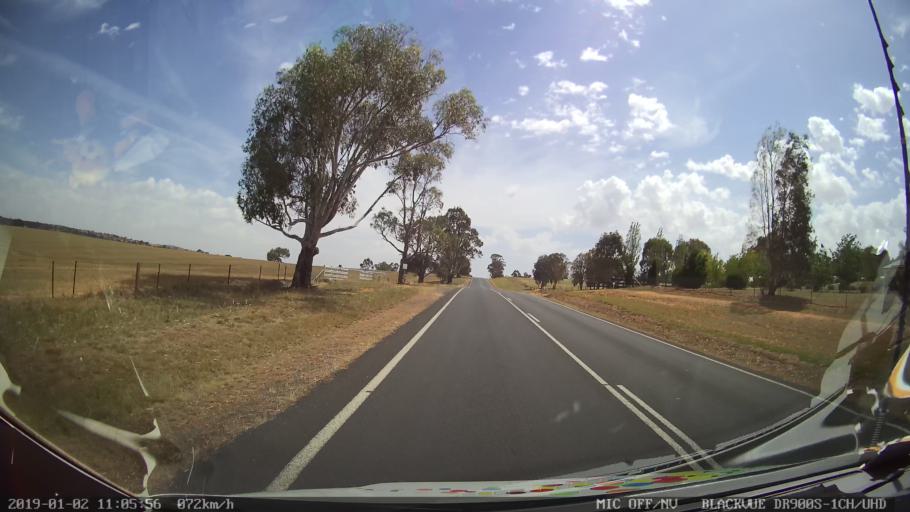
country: AU
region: New South Wales
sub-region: Young
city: Young
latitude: -34.5594
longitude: 148.3547
